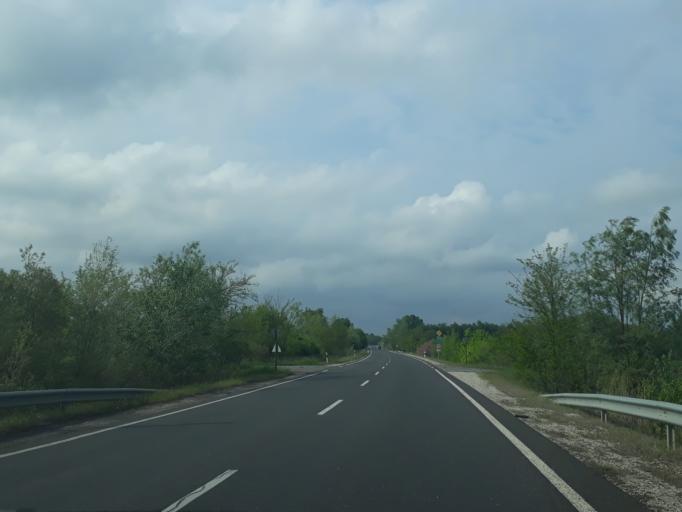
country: HU
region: Szabolcs-Szatmar-Bereg
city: Nyirtass
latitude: 48.0884
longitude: 21.9870
